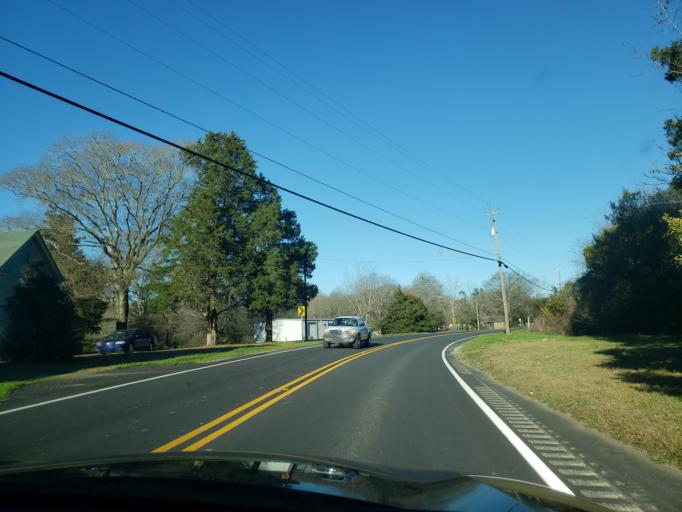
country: US
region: Alabama
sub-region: Macon County
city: Tuskegee
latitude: 32.5636
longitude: -85.6789
